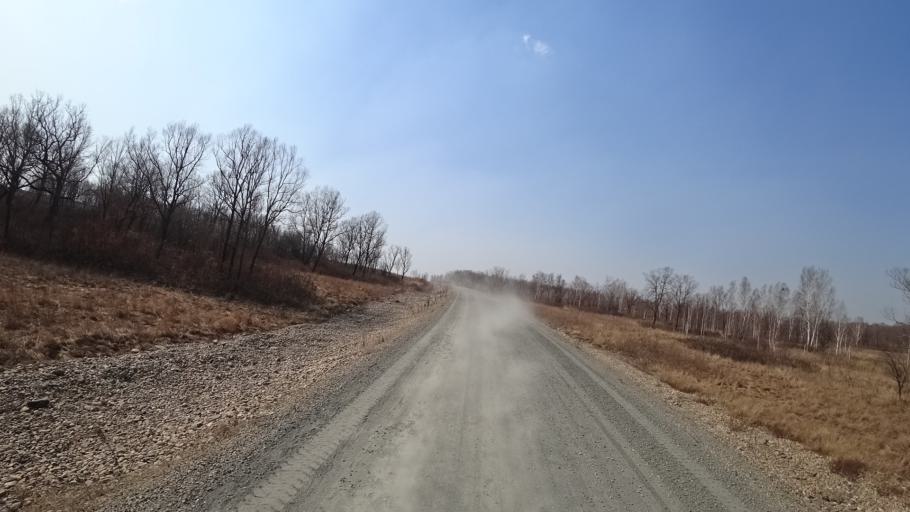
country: RU
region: Amur
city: Novobureyskiy
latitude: 49.8261
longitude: 129.9937
